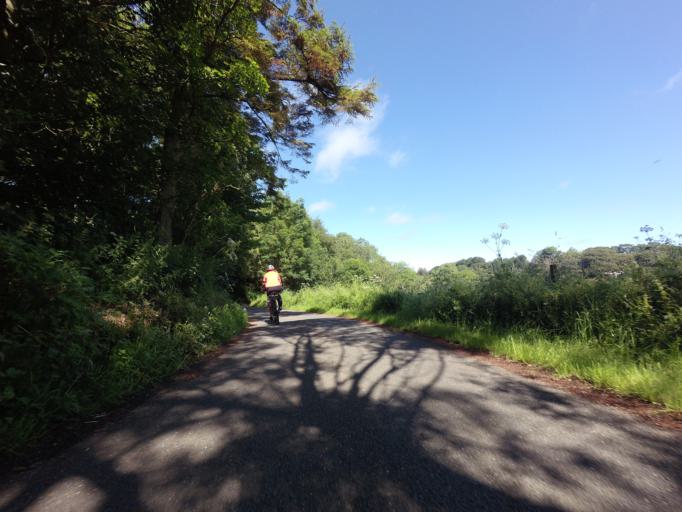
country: GB
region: Scotland
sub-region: Aberdeenshire
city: Banff
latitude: 57.6092
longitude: -2.5114
